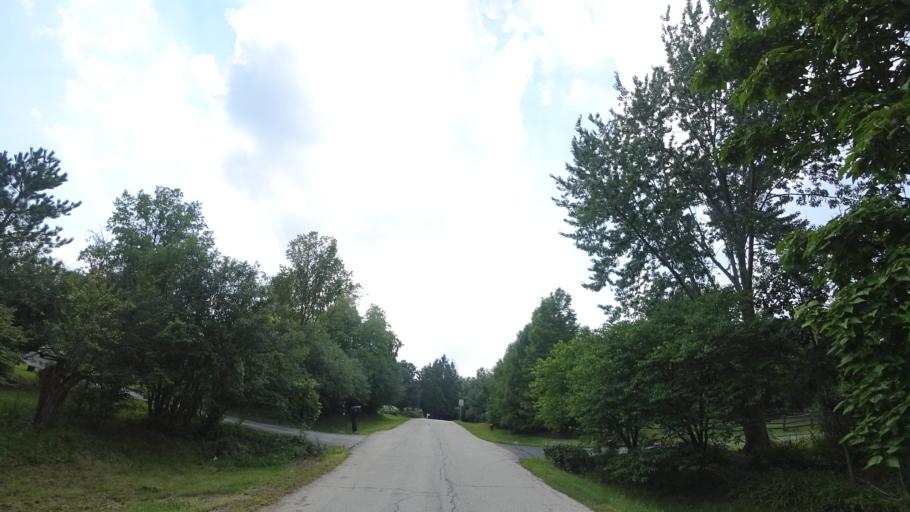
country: US
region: Illinois
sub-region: Will County
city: Goodings Grove
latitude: 41.6566
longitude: -87.8996
